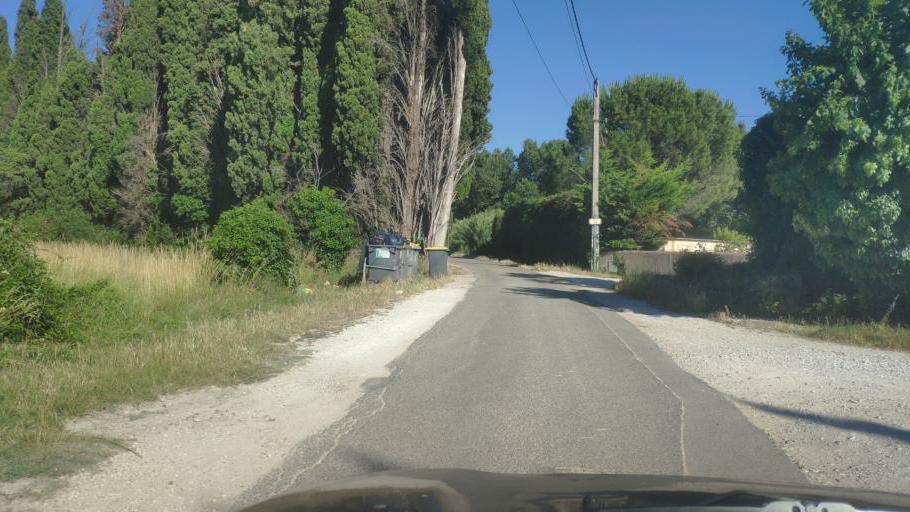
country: FR
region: Provence-Alpes-Cote d'Azur
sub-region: Departement du Vaucluse
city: Aubignan
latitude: 44.0894
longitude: 5.0383
